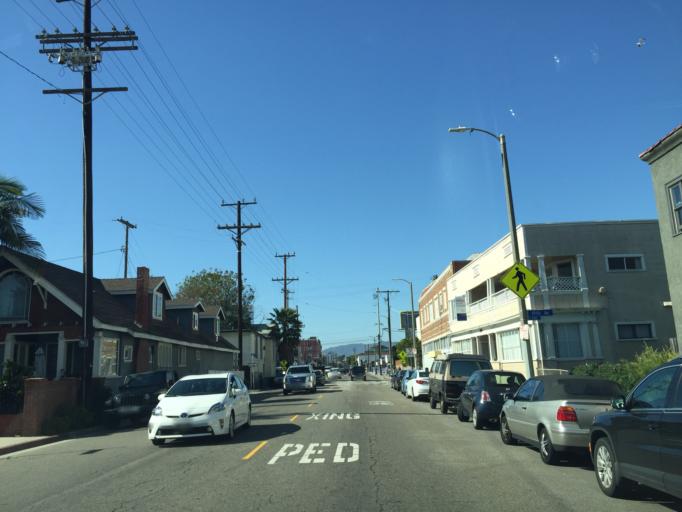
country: US
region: California
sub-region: Los Angeles County
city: Marina del Rey
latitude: 33.9860
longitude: -118.4709
